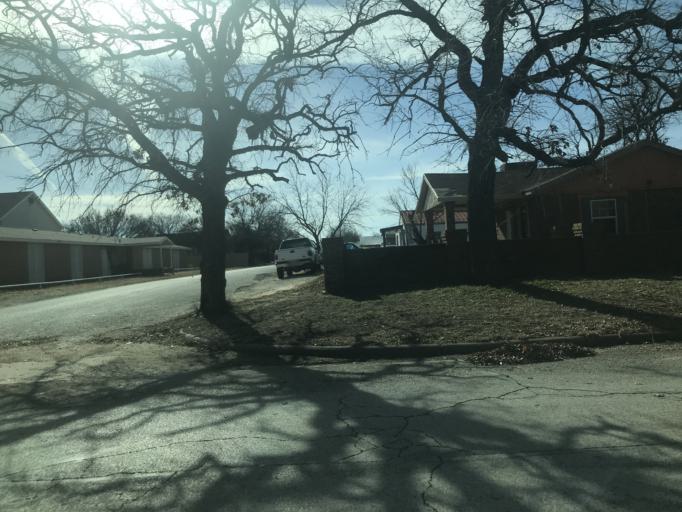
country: US
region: Texas
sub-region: Taylor County
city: Abilene
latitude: 32.4868
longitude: -99.7383
